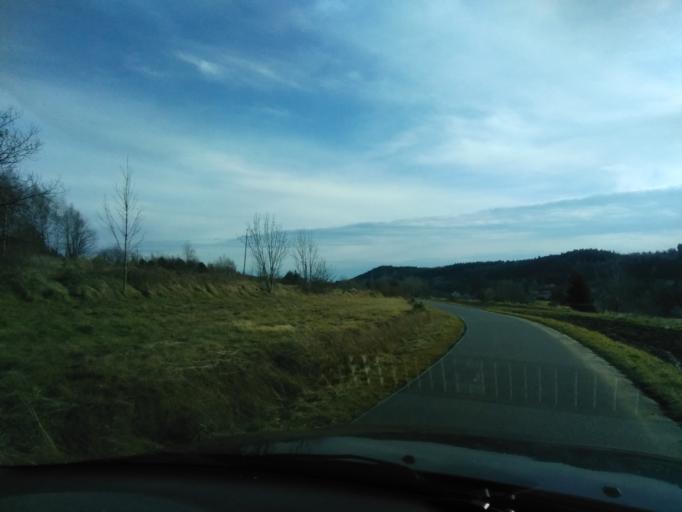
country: PL
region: Subcarpathian Voivodeship
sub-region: Powiat krosnienski
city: Korczyna
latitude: 49.7492
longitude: 21.7939
